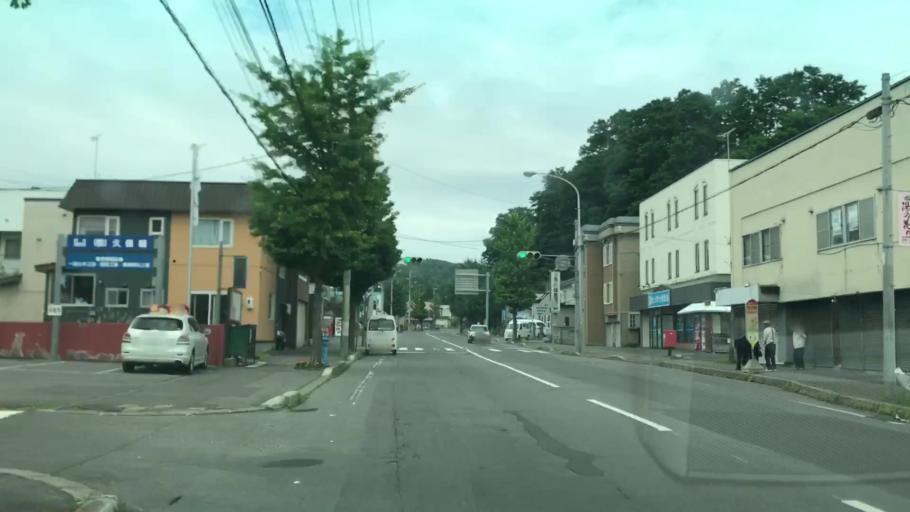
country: JP
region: Hokkaido
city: Otaru
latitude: 43.2096
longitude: 140.9713
